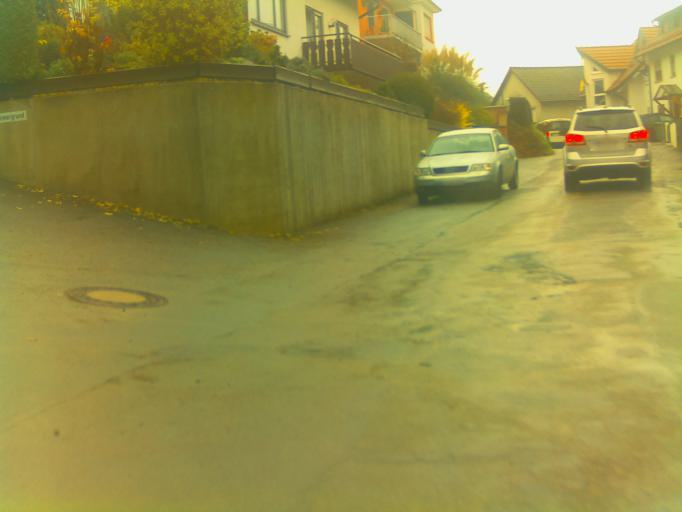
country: DE
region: Baden-Wuerttemberg
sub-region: Karlsruhe Region
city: Schonau
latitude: 49.4408
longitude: 8.8081
